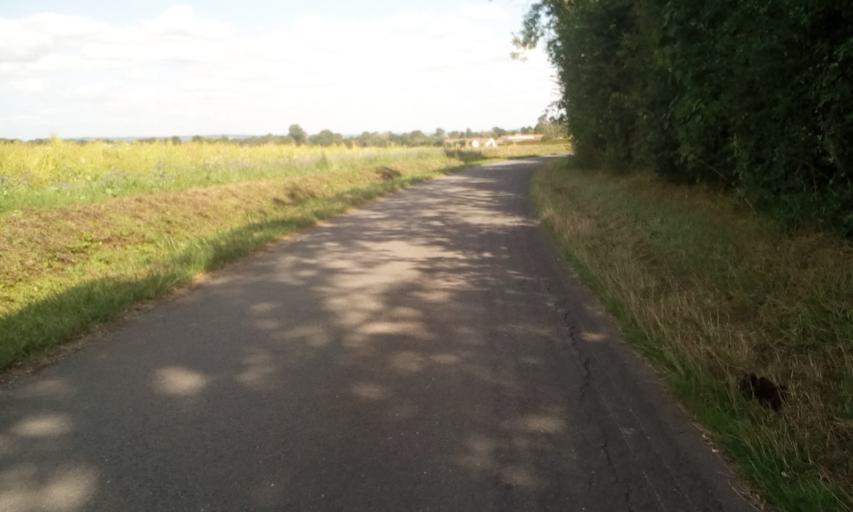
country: FR
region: Lower Normandy
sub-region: Departement du Calvados
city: Argences
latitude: 49.1321
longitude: -0.1218
